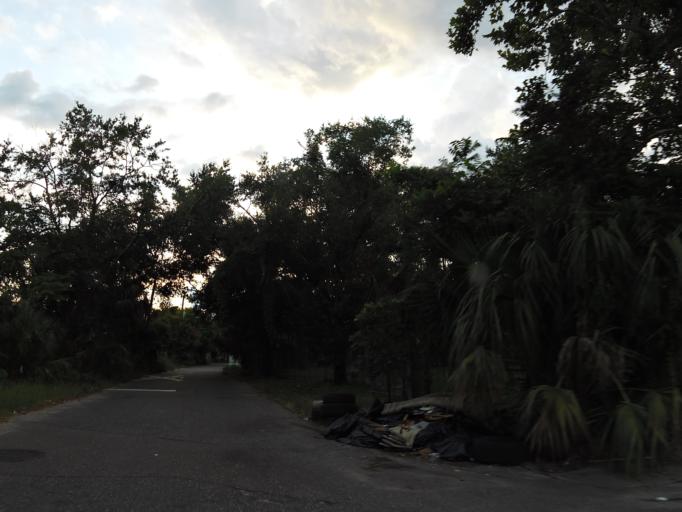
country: US
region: Florida
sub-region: Duval County
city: Jacksonville
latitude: 30.3242
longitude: -81.6885
